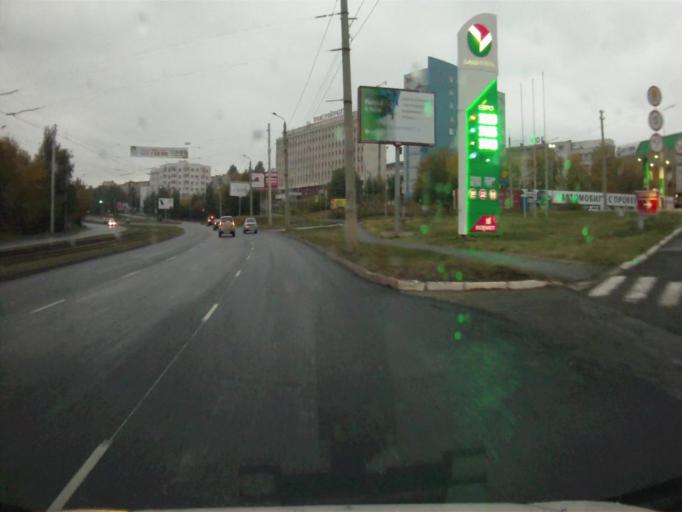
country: RU
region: Chelyabinsk
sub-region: Gorod Chelyabinsk
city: Chelyabinsk
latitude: 55.1886
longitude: 61.3597
